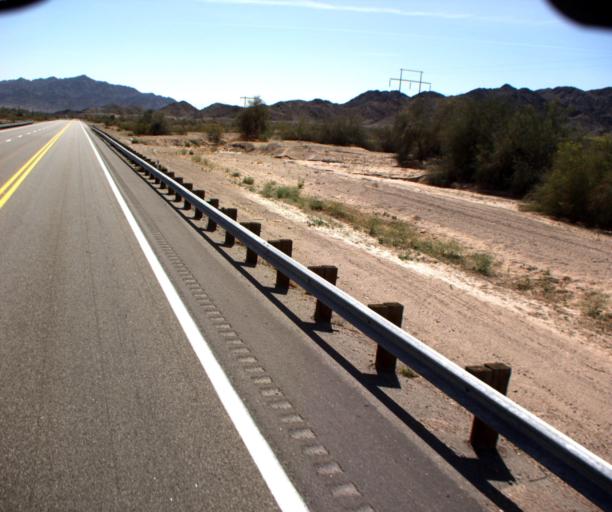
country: US
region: Arizona
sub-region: Yuma County
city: Fortuna Foothills
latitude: 32.8000
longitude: -114.3808
